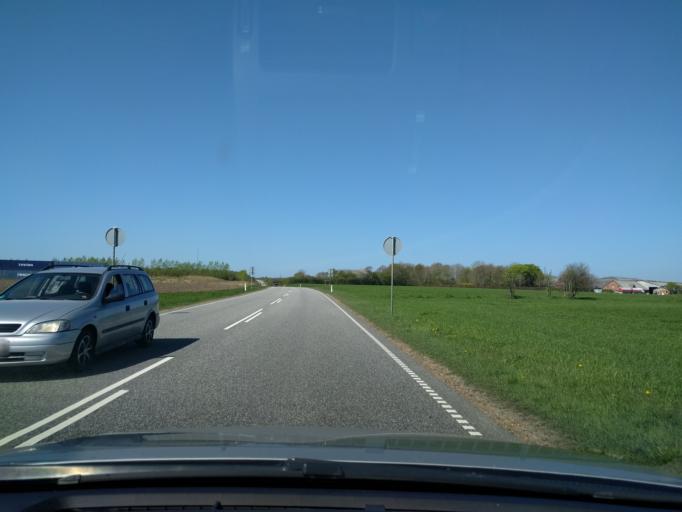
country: DK
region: Central Jutland
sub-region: Ringkobing-Skjern Kommune
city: Videbaek
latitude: 56.0989
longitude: 8.6290
